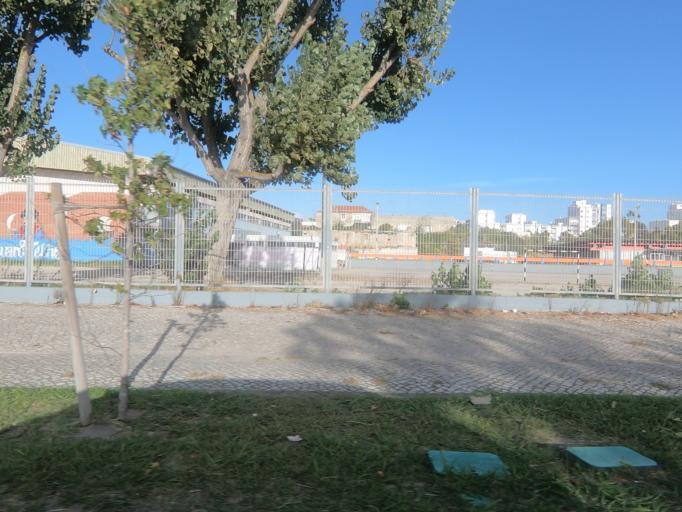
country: PT
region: Setubal
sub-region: Barreiro
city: Barreiro
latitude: 38.6639
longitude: -9.0554
